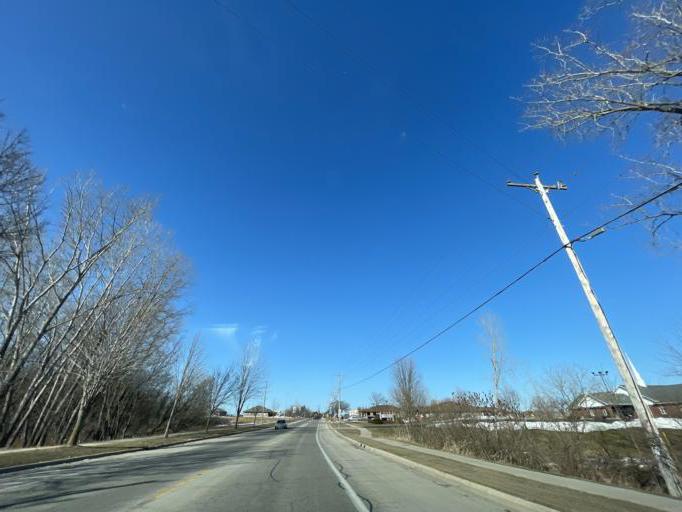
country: US
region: Wisconsin
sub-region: Brown County
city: Howard
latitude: 44.5879
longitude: -88.0843
